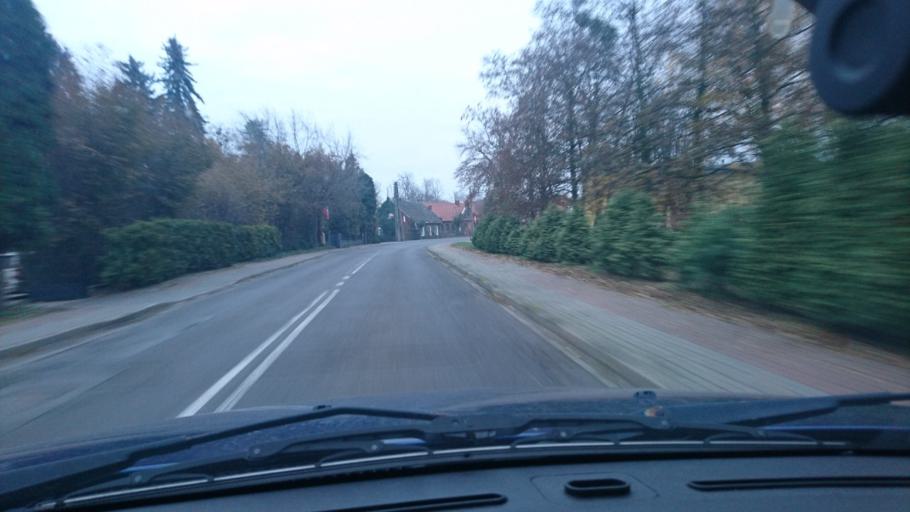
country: PL
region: Greater Poland Voivodeship
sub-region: Powiat ostrowski
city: Odolanow
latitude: 51.5729
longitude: 17.6682
